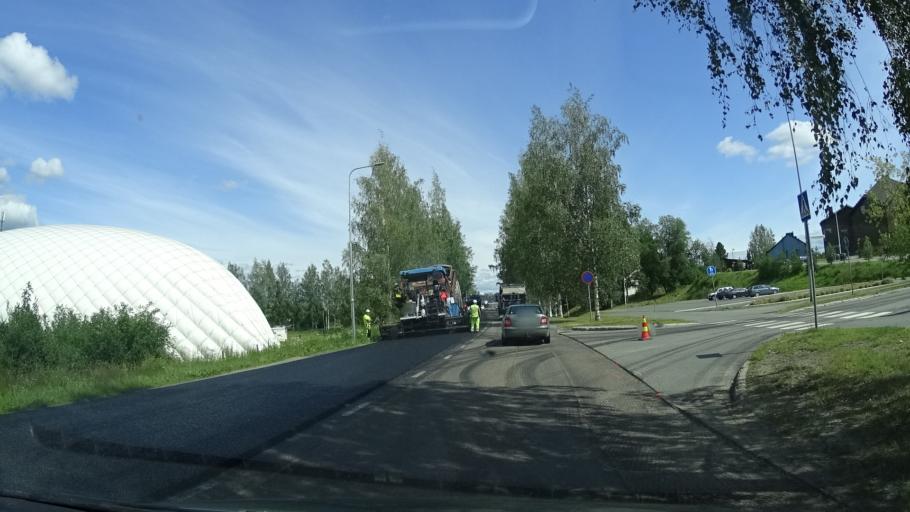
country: FI
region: Central Finland
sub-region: Jyvaeskylae
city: Jyvaeskylae
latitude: 62.2444
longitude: 25.7177
